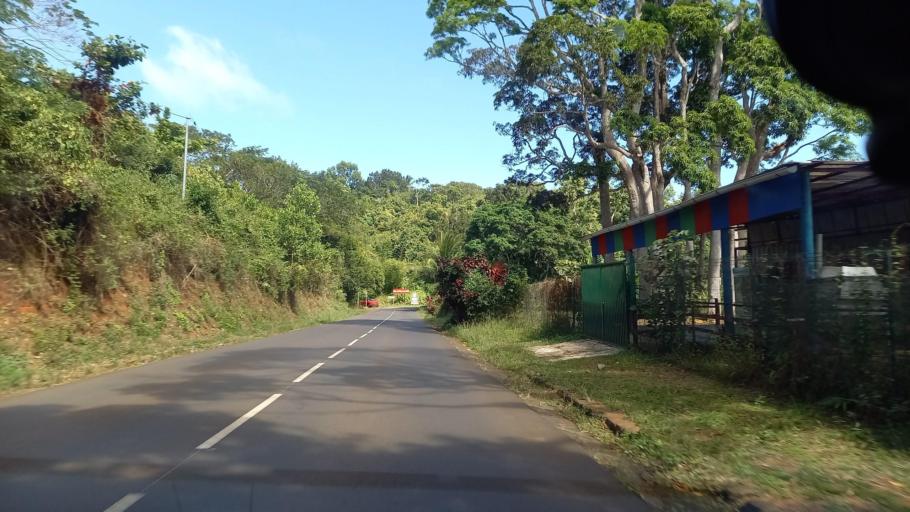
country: YT
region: Dembeni
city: Dembeni
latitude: -12.7893
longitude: 45.1638
